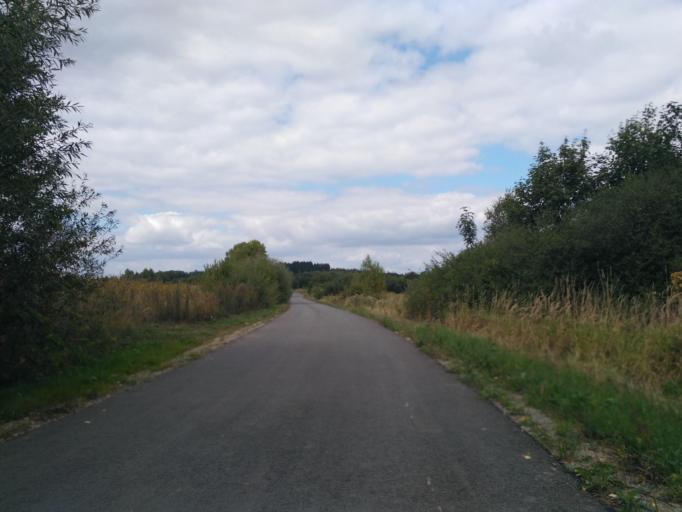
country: PL
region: Subcarpathian Voivodeship
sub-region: Powiat rzeszowski
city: Dynow
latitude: 49.7717
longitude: 22.2829
